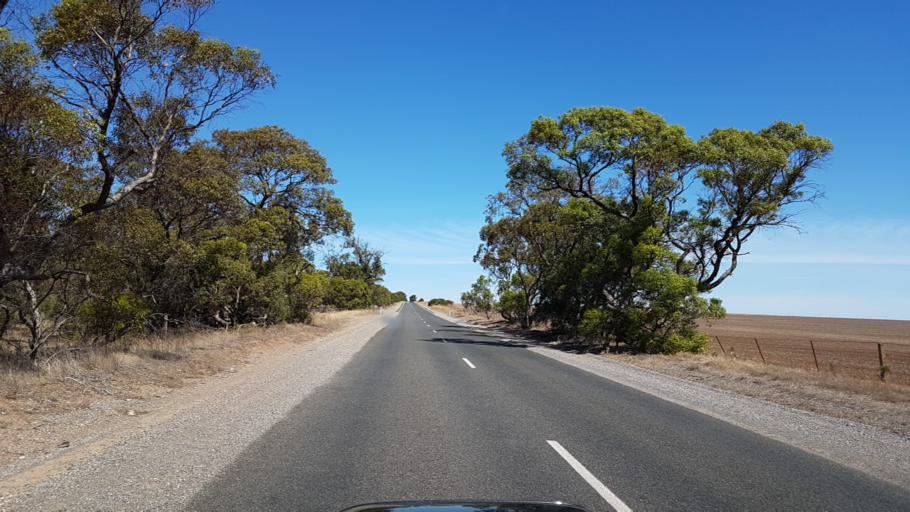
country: AU
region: South Australia
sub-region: Yorke Peninsula
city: Maitland
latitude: -34.3400
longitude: 137.6576
